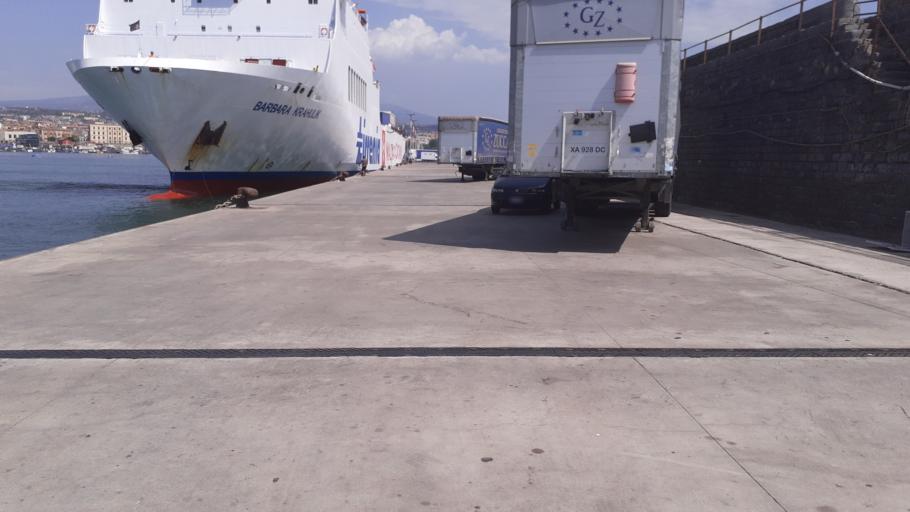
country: IT
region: Sicily
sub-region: Catania
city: Catania
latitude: 37.4953
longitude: 15.0994
